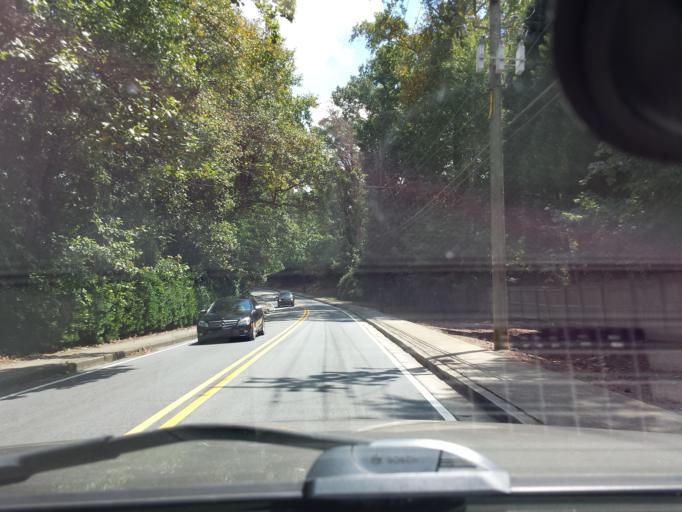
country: US
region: Georgia
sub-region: Cobb County
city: Vinings
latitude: 33.9379
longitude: -84.4590
